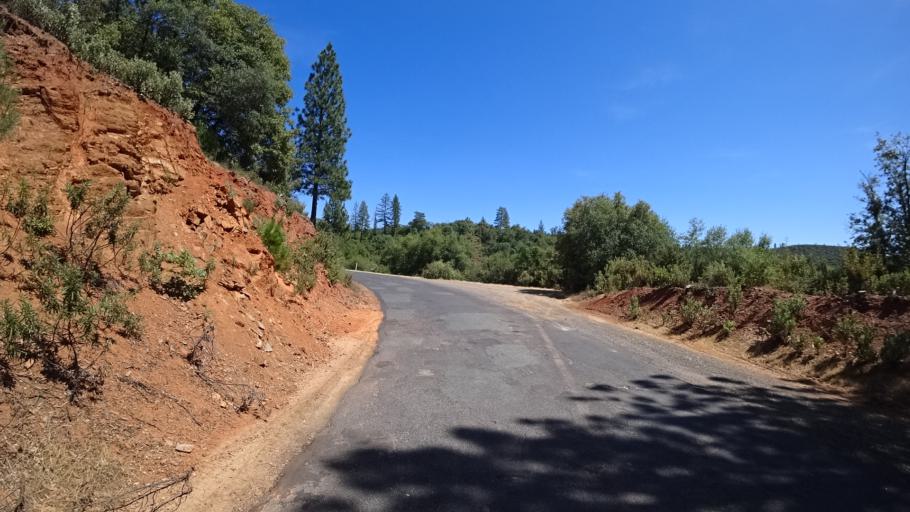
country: US
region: California
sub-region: Calaveras County
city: Murphys
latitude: 38.1724
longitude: -120.4591
